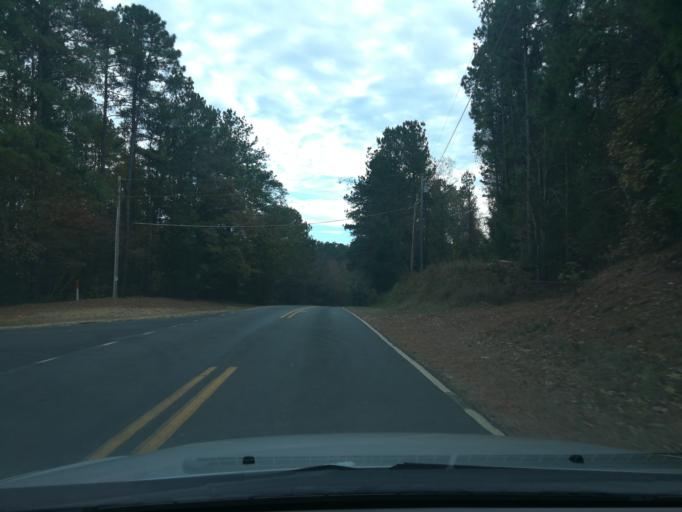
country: US
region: North Carolina
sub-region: Orange County
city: Hillsborough
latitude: 36.0211
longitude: -79.0400
